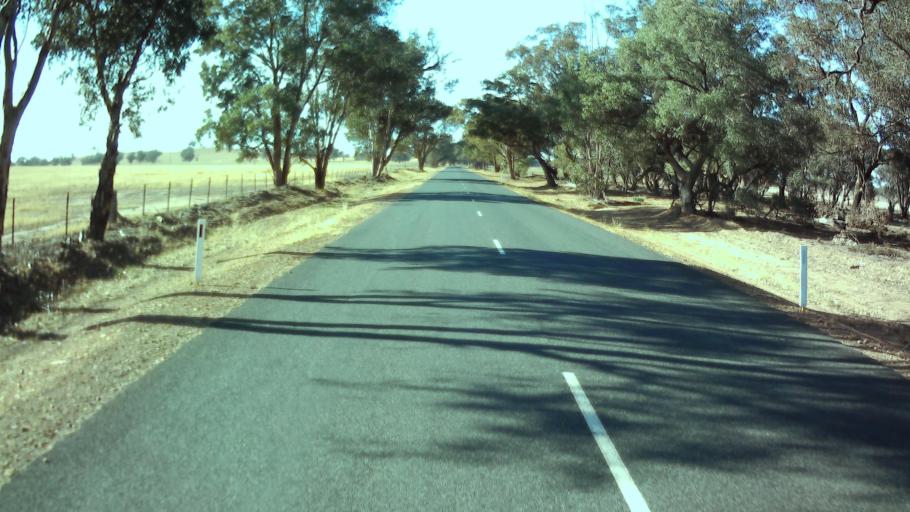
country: AU
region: New South Wales
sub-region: Weddin
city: Grenfell
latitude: -33.9531
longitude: 148.1388
